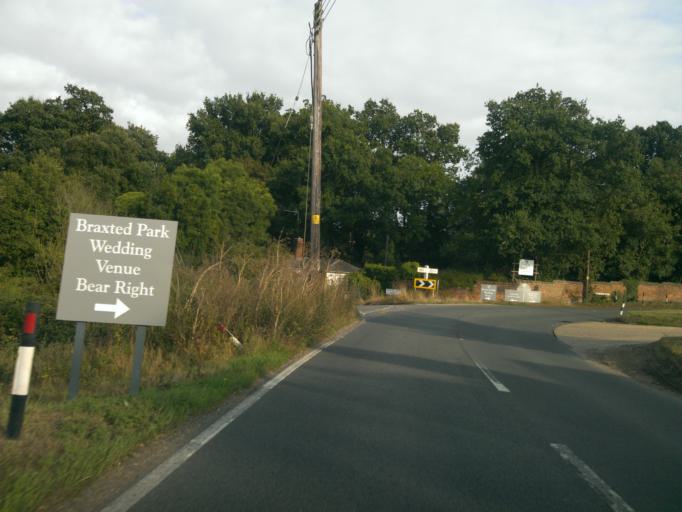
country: GB
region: England
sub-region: Essex
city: Great Totham
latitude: 51.8093
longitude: 0.6774
